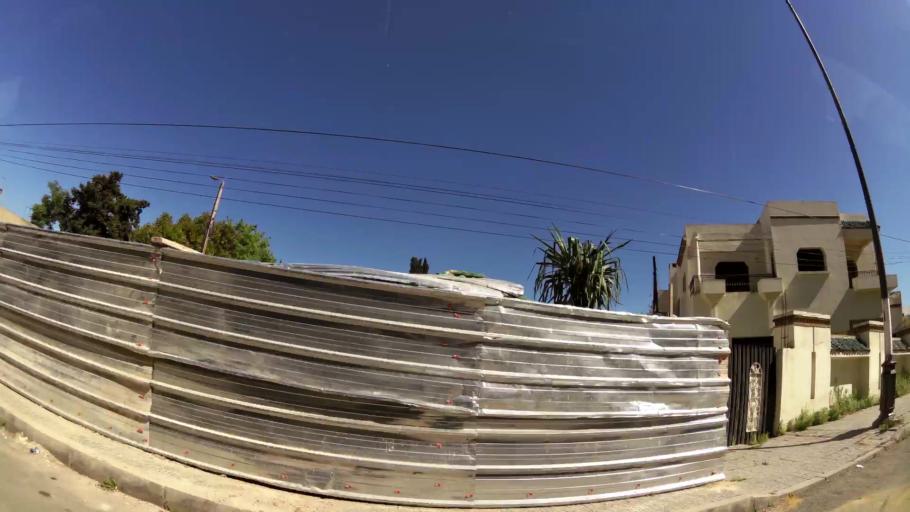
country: MA
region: Fes-Boulemane
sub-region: Fes
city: Fes
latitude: 34.0256
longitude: -4.9953
